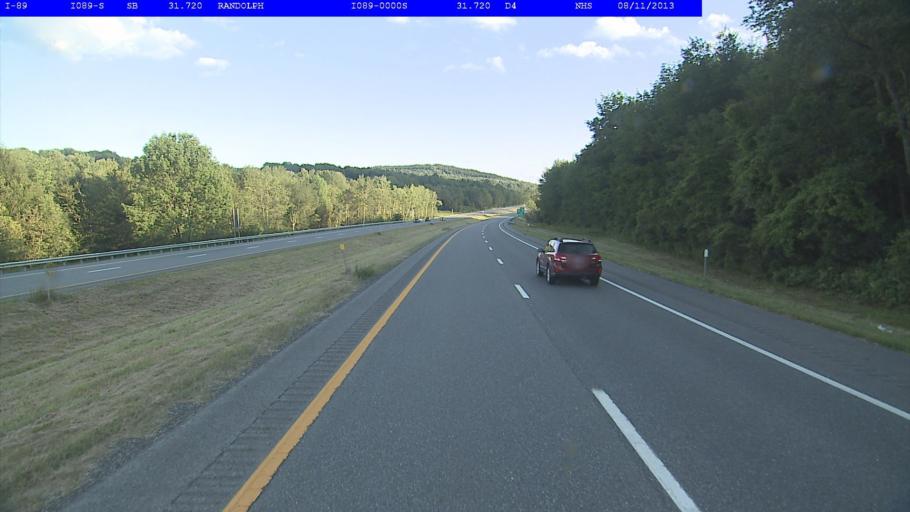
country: US
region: Vermont
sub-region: Orange County
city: Randolph
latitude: 43.9570
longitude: -72.6225
